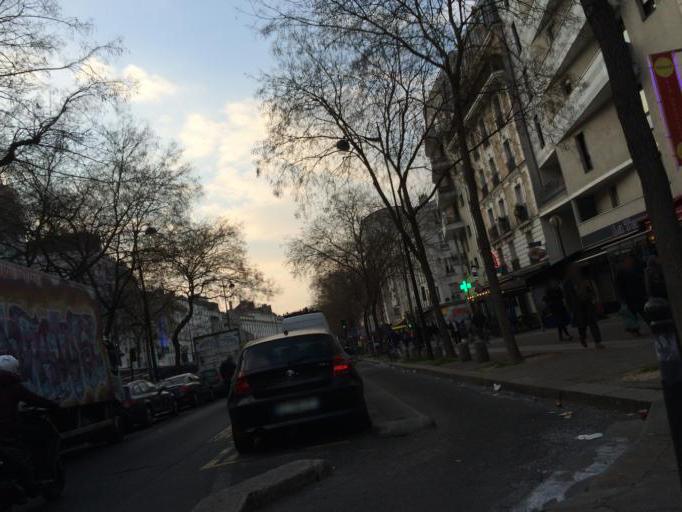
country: FR
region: Ile-de-France
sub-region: Departement de Seine-Saint-Denis
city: Le Pre-Saint-Gervais
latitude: 48.8695
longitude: 2.3800
